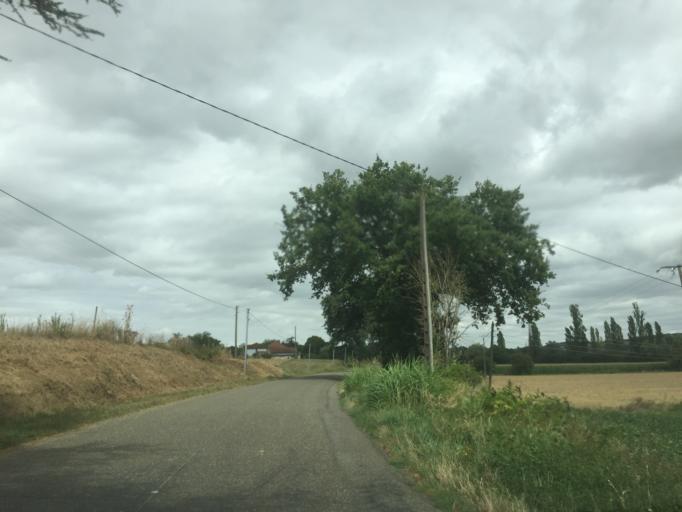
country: FR
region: Midi-Pyrenees
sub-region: Departement du Gers
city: Mirande
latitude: 43.6075
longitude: 0.3379
